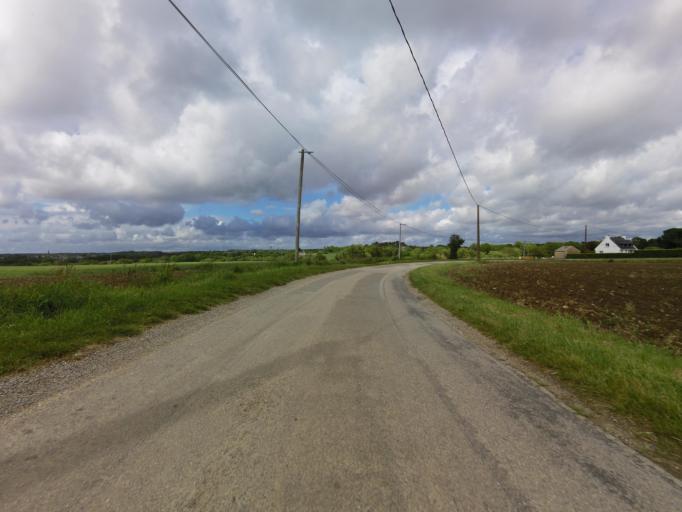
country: FR
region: Brittany
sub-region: Departement du Morbihan
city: Plougoumelen
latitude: 47.6360
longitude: -2.9142
